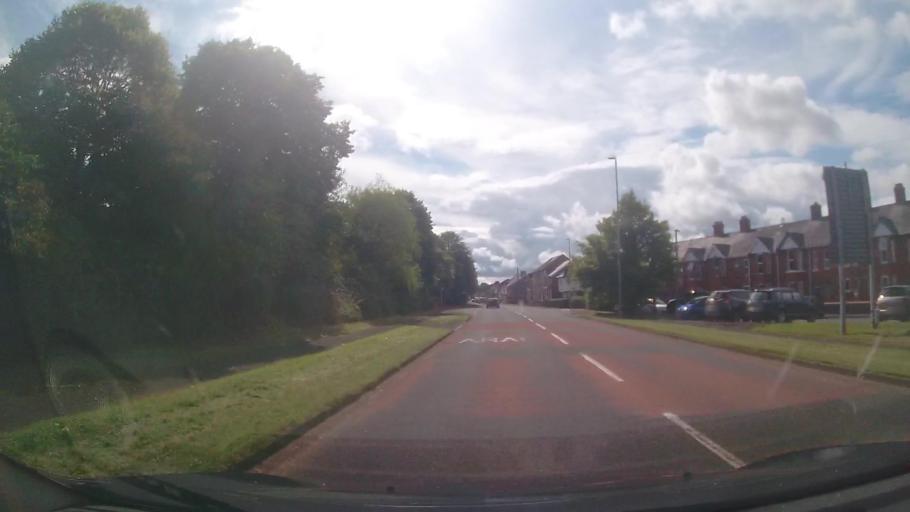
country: GB
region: Wales
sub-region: Sir Powys
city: Llandrindod Wells
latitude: 52.2526
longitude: -3.3731
